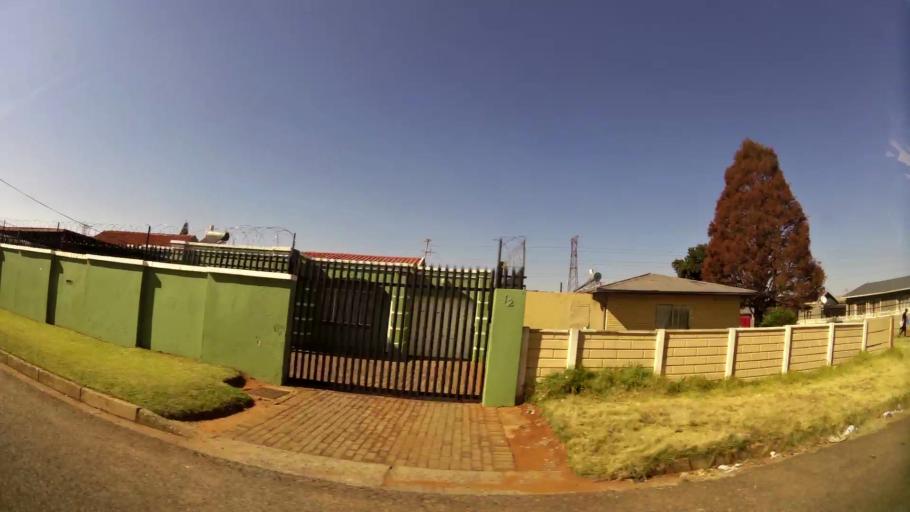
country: ZA
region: Gauteng
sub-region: City of Johannesburg Metropolitan Municipality
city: Roodepoort
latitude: -26.1761
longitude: 27.9533
